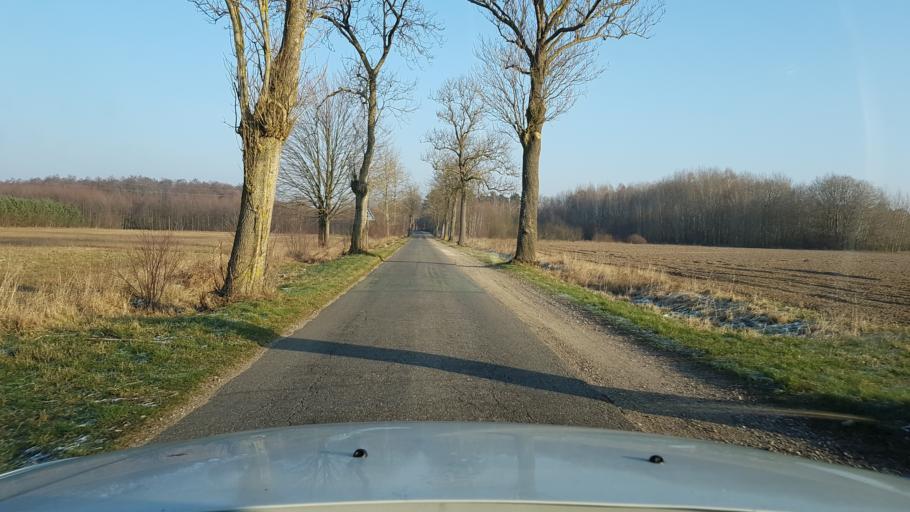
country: PL
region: West Pomeranian Voivodeship
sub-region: Powiat bialogardzki
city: Bialogard
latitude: 54.0572
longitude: 16.0775
